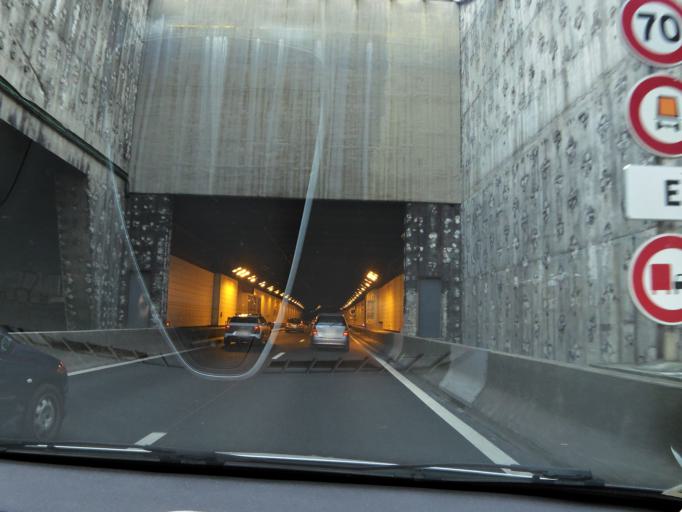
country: FR
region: Rhone-Alpes
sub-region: Departement du Rhone
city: Tassin-la-Demi-Lune
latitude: 45.7635
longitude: 4.8027
